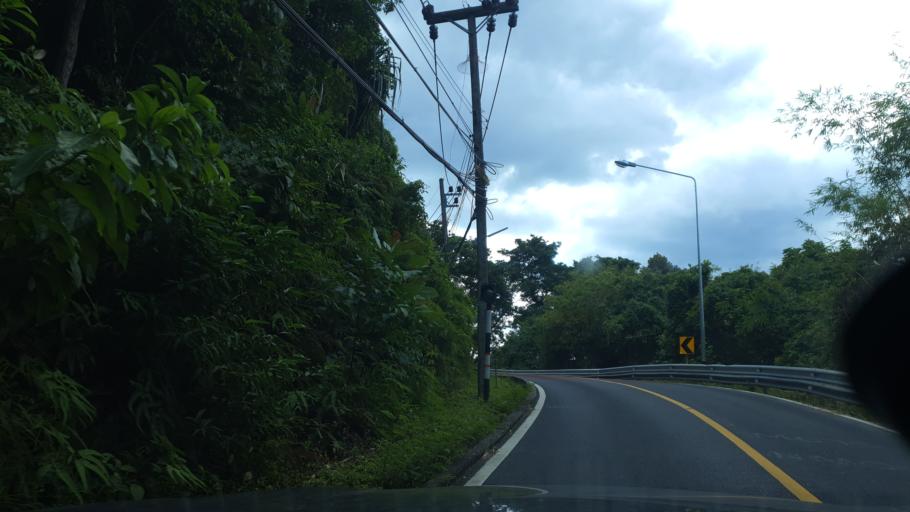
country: TH
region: Phuket
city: Thalang
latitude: 8.0449
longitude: 98.2772
